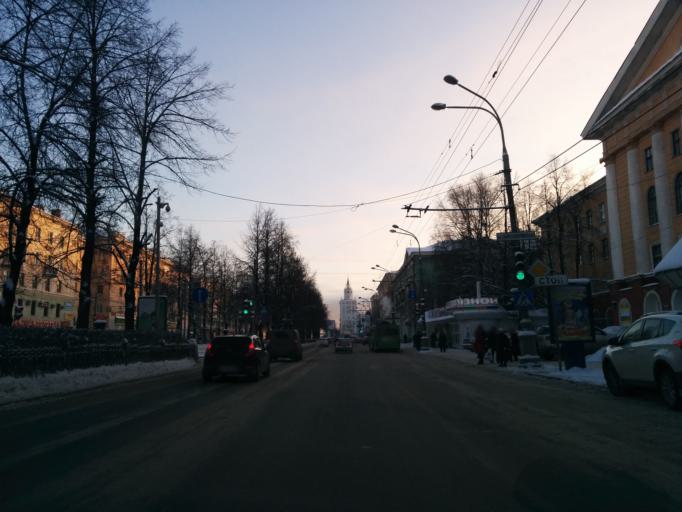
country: RU
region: Perm
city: Perm
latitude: 57.9989
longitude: 56.2504
